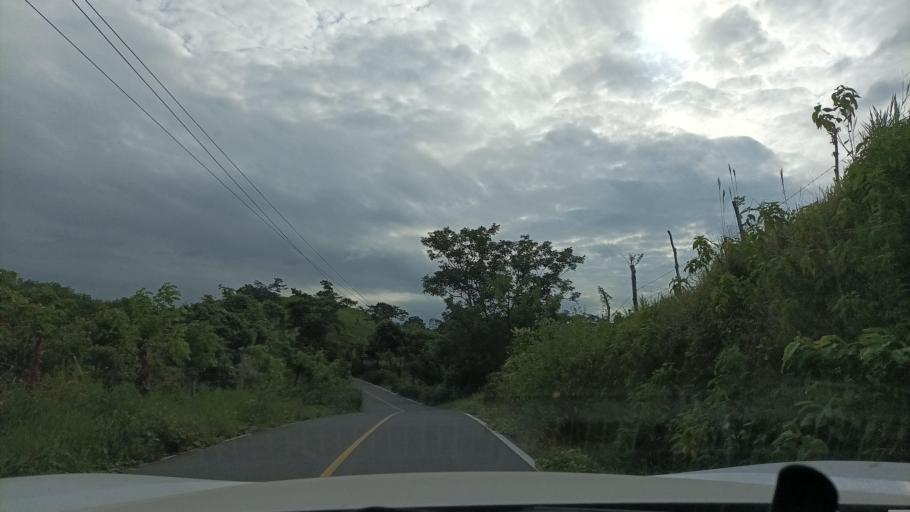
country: MX
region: Veracruz
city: Hidalgotitlan
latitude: 17.6901
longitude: -94.4592
